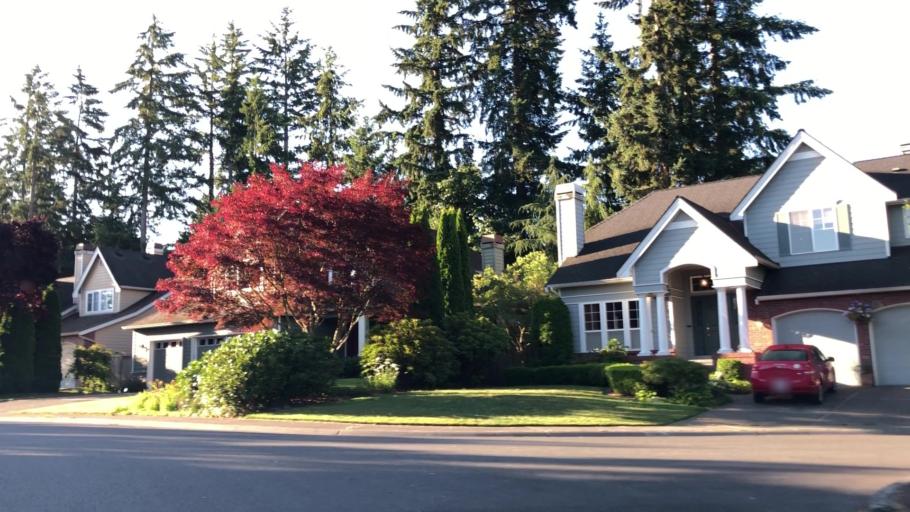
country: US
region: Washington
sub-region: King County
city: Redmond
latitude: 47.6970
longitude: -122.1156
